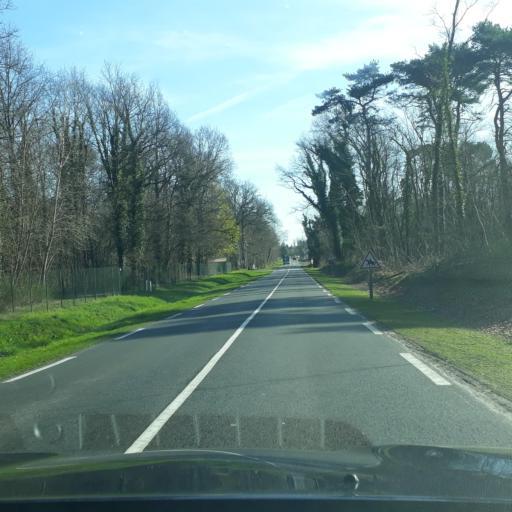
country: FR
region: Ile-de-France
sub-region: Departement de l'Essonne
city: Cerny
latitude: 48.4788
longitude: 2.3179
